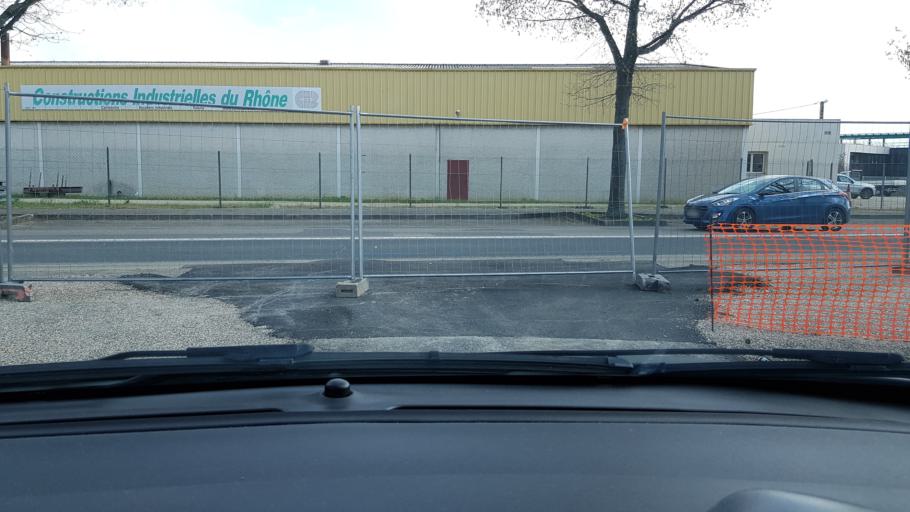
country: FR
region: Rhone-Alpes
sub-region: Departement du Rhone
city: Brignais
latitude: 45.6677
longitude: 4.7599
